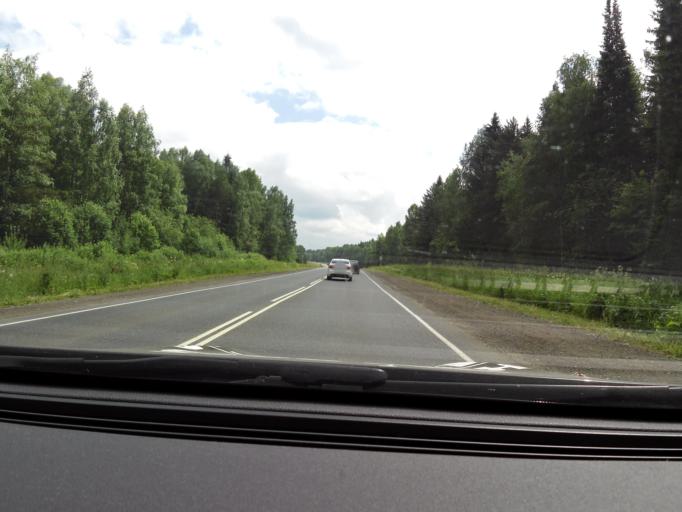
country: RU
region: Perm
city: Kungur
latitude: 57.4267
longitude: 56.8347
